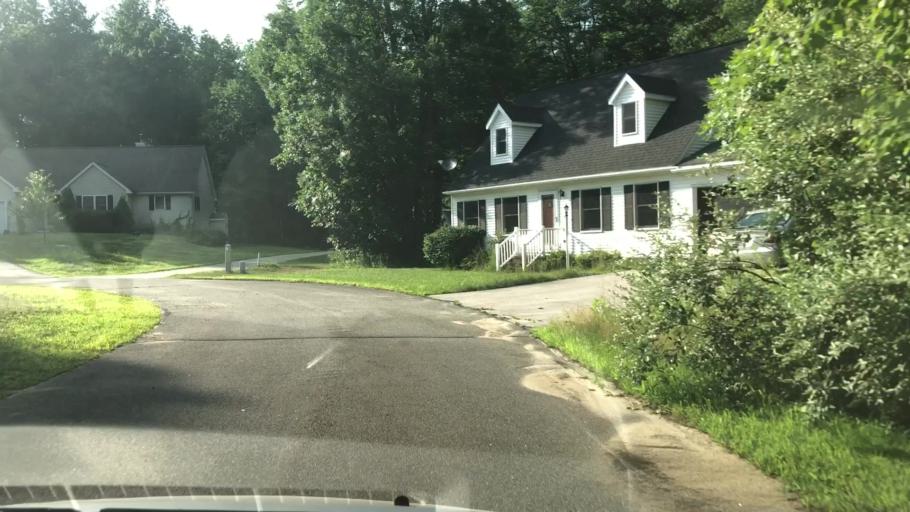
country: US
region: New Hampshire
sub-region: Hillsborough County
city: Milford
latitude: 42.8419
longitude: -71.6248
